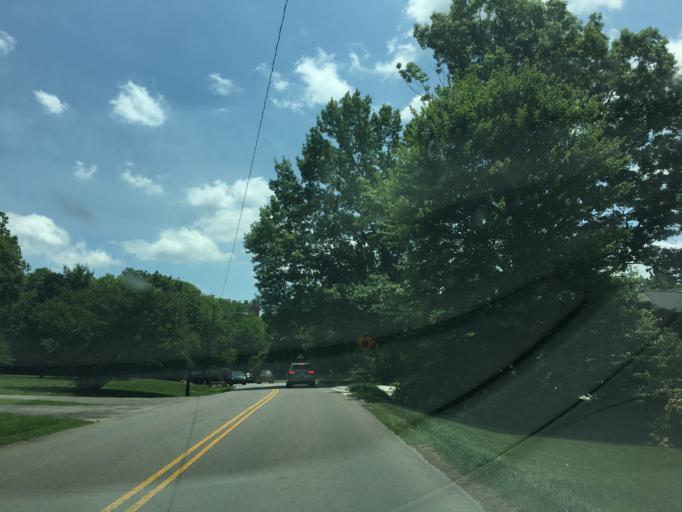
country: US
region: Tennessee
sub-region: Davidson County
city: Belle Meade
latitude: 36.1106
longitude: -86.8224
